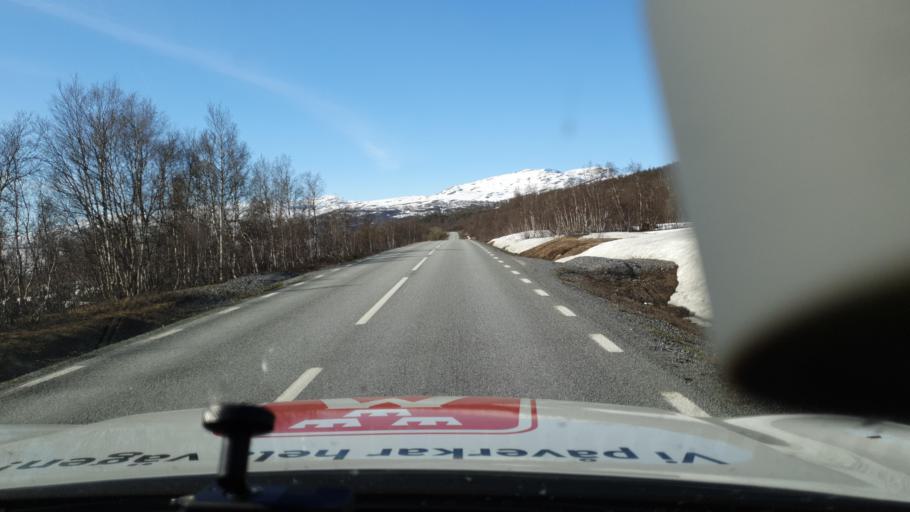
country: NO
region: Nordland
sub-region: Rana
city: Mo i Rana
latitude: 66.0752
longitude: 14.8715
